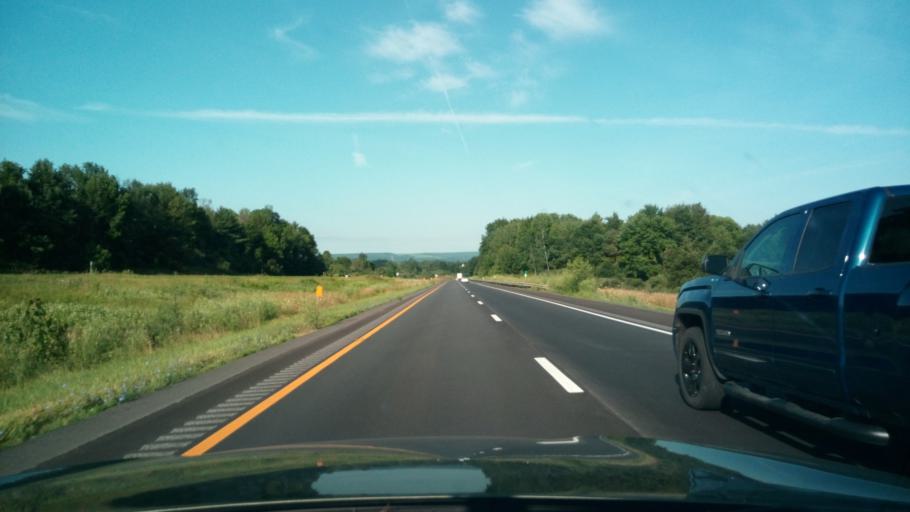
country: US
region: New York
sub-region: Livingston County
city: Dansville
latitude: 42.5323
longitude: -77.6426
